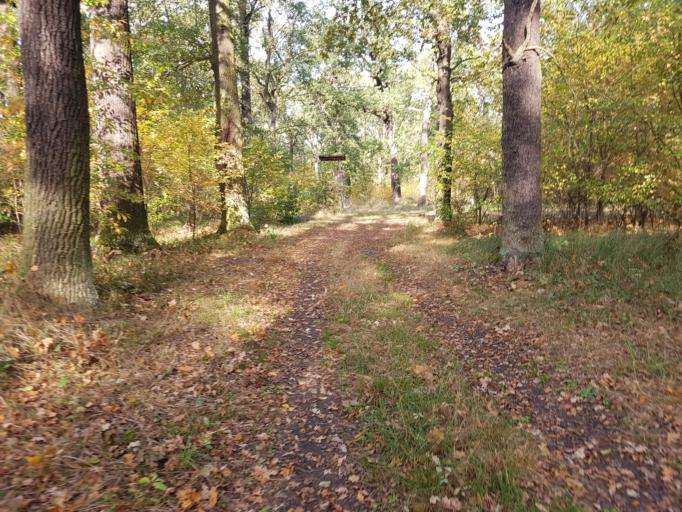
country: DE
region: Brandenburg
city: Schilda
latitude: 51.5919
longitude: 13.3366
